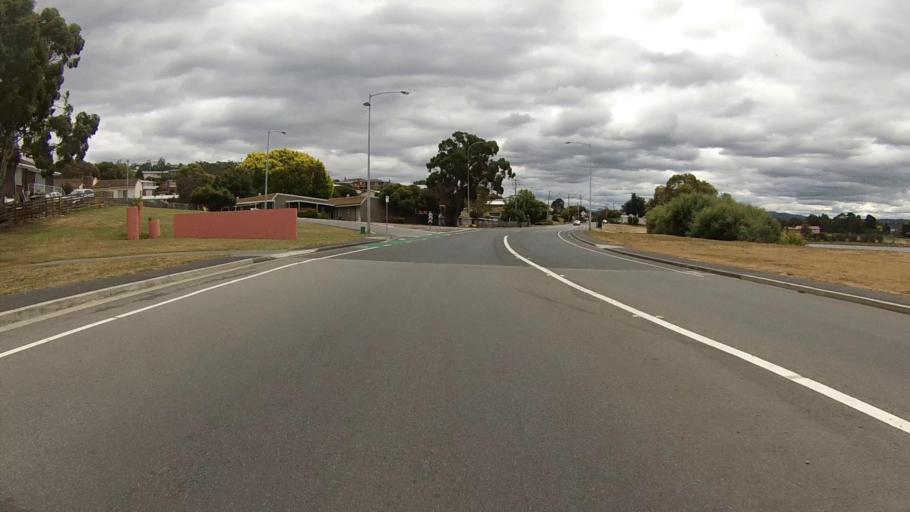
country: AU
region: Tasmania
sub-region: Glenorchy
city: Claremont
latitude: -42.7868
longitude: 147.2518
